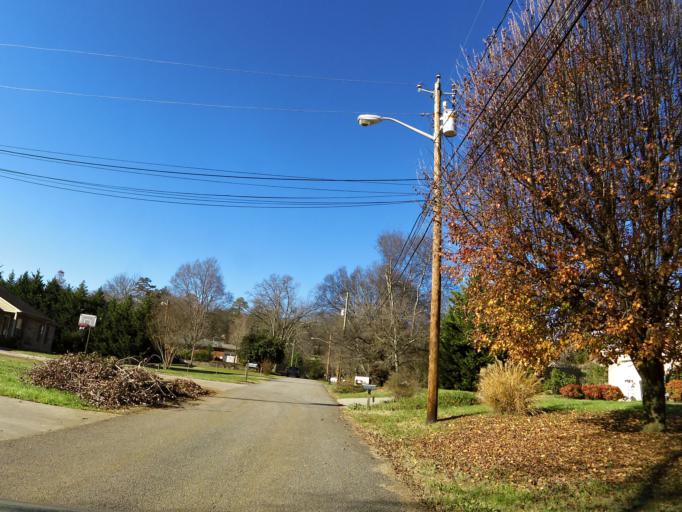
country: US
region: Tennessee
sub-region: Knox County
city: Knoxville
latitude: 36.0244
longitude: -83.9523
